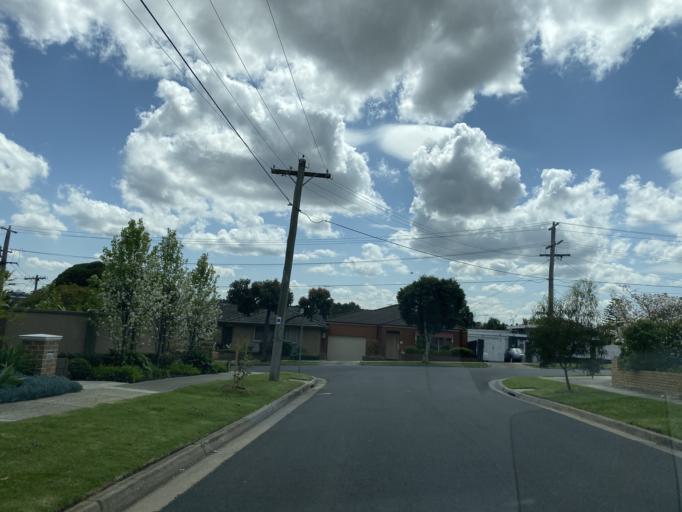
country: AU
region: Victoria
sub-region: Monash
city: Ashwood
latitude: -37.8579
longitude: 145.1054
